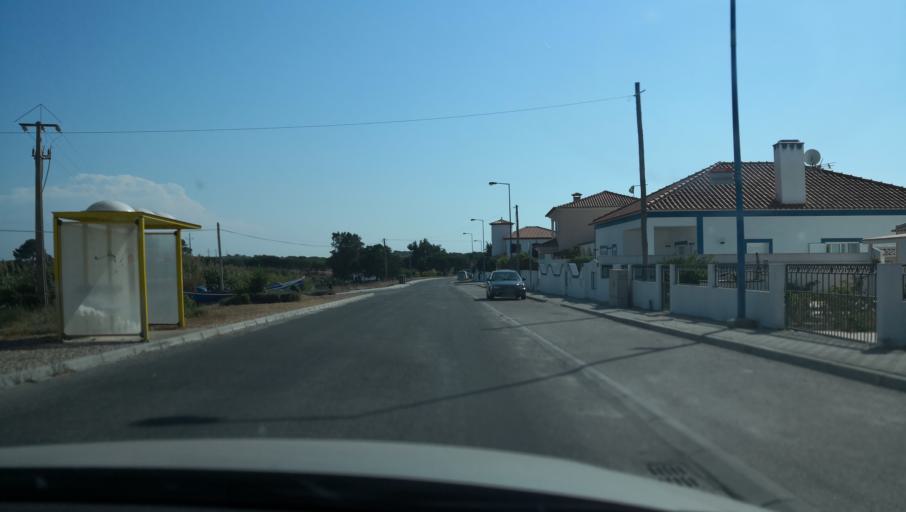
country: PT
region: Setubal
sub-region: Setubal
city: Setubal
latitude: 38.4079
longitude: -8.7522
